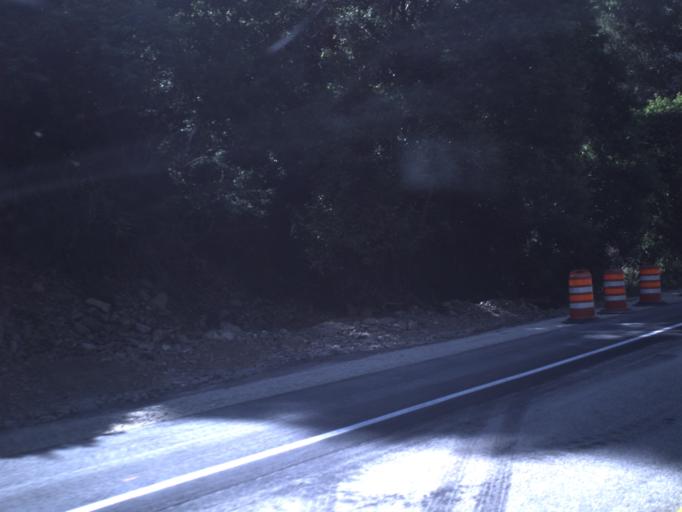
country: US
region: Utah
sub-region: Wasatch County
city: Heber
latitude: 40.3849
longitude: -111.3020
